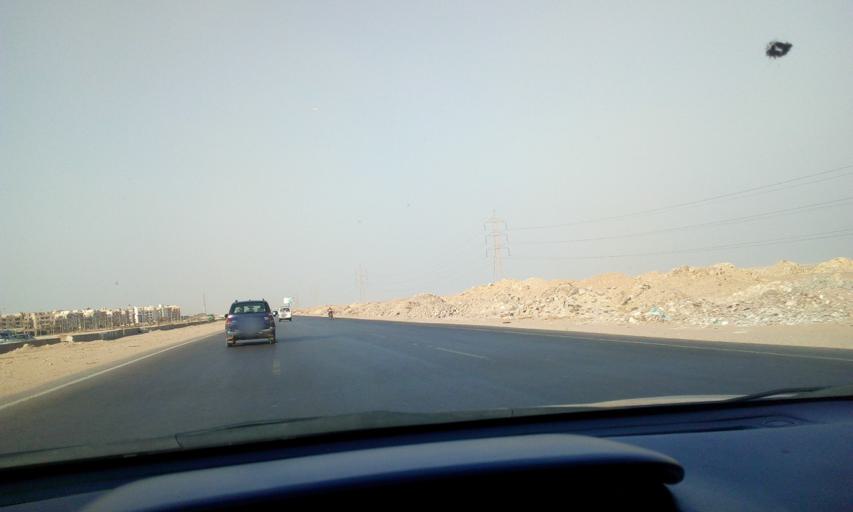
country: EG
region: Al Jizah
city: Madinat Sittah Uktubar
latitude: 29.8880
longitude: 31.0808
